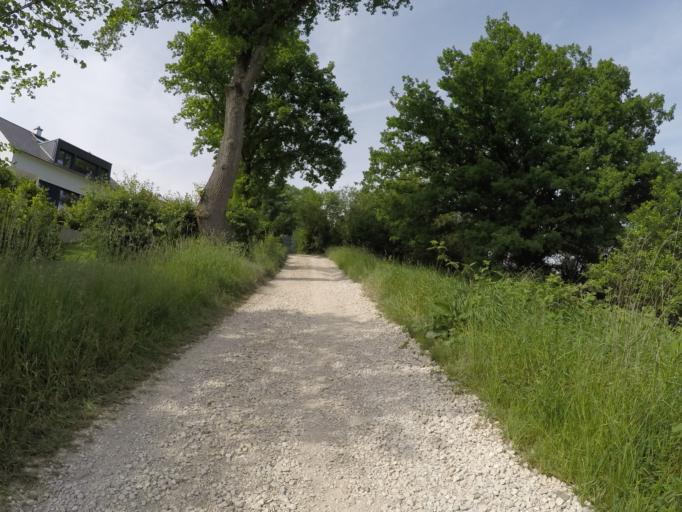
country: DE
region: Baden-Wuerttemberg
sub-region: Regierungsbezirk Stuttgart
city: Kongen
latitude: 48.6875
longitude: 9.3721
